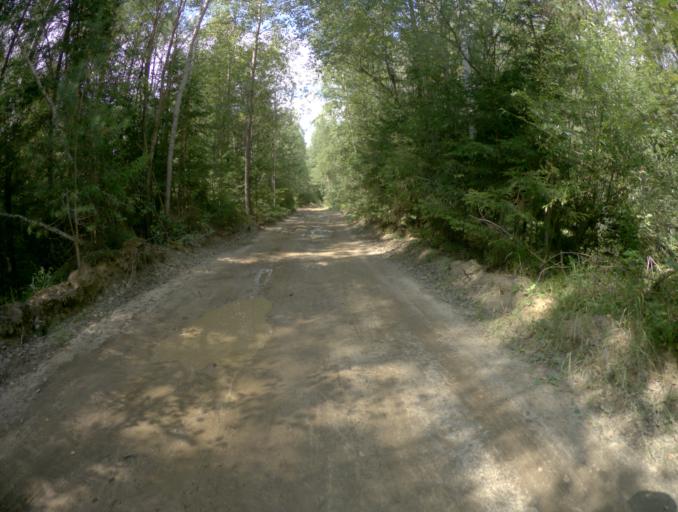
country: RU
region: Vladimir
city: Raduzhnyy
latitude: 55.9670
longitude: 40.2362
